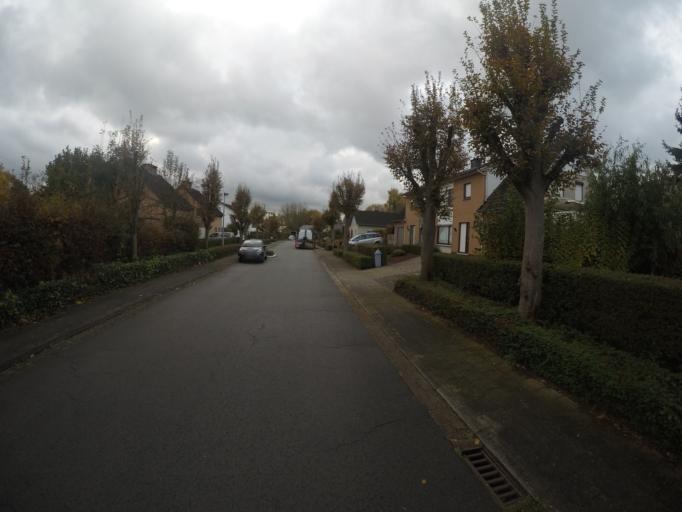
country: BE
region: Flanders
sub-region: Provincie Oost-Vlaanderen
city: Hamme
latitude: 51.1166
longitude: 4.1298
